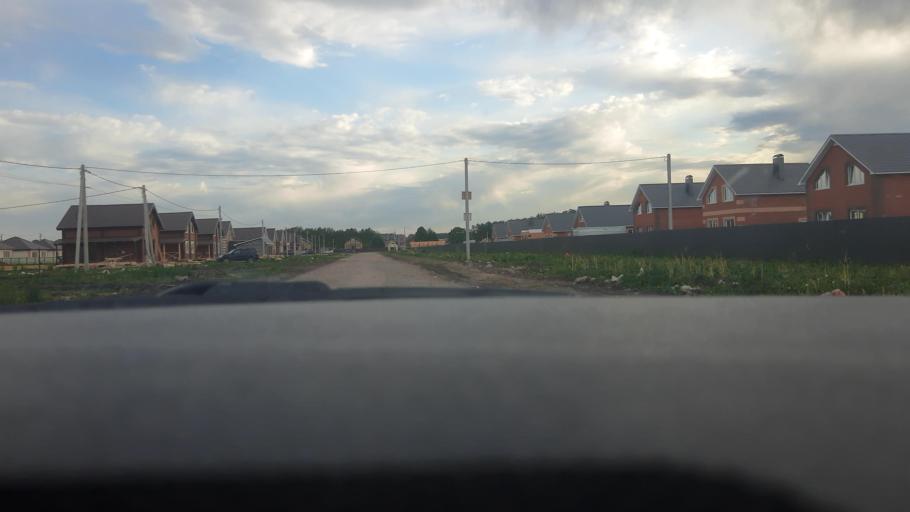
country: RU
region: Bashkortostan
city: Kabakovo
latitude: 54.6294
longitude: 56.1364
